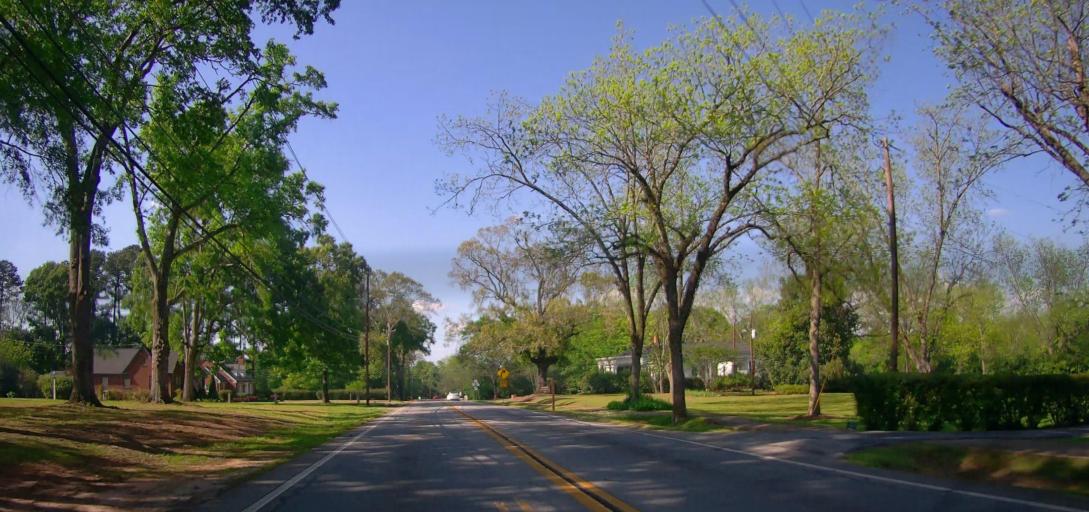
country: US
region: Georgia
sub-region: Morgan County
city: Madison
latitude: 33.5836
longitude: -83.4776
